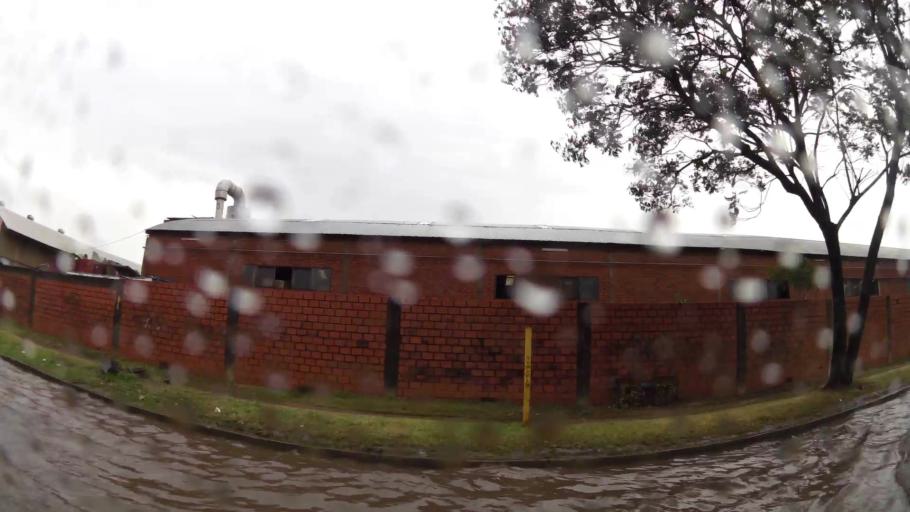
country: BO
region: Santa Cruz
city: Santa Cruz de la Sierra
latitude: -17.7612
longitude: -63.1402
